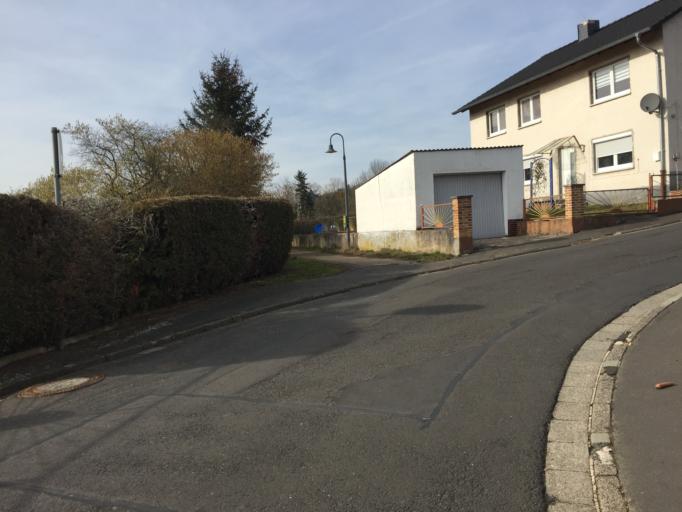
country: DE
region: Hesse
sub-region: Regierungsbezirk Giessen
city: Fronhausen
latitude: 50.6829
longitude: 8.6860
